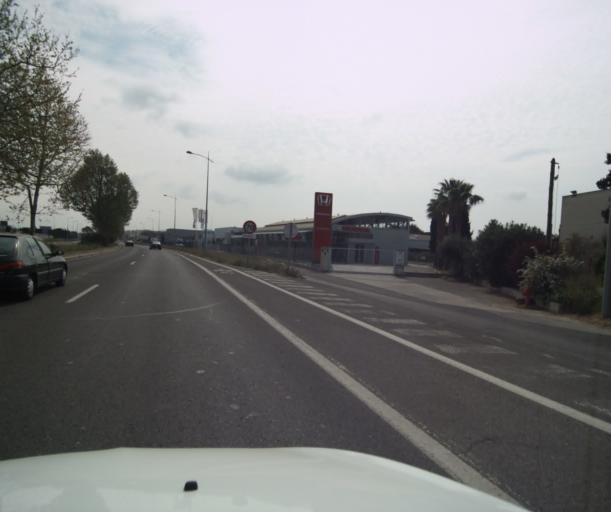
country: FR
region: Provence-Alpes-Cote d'Azur
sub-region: Departement du Var
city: La Garde
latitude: 43.1368
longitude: 6.0279
